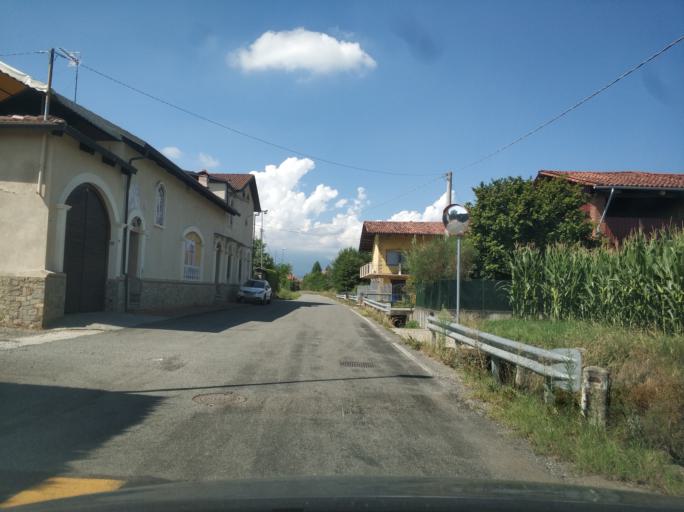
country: IT
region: Piedmont
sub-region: Provincia di Torino
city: Rivarolo Canavese
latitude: 45.3117
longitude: 7.7237
